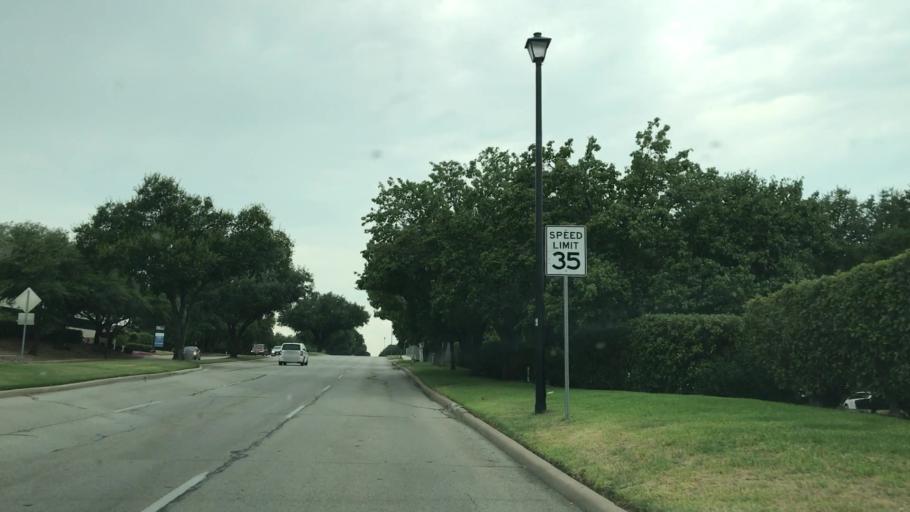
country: US
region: Texas
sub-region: Dallas County
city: Irving
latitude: 32.8851
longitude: -96.9660
